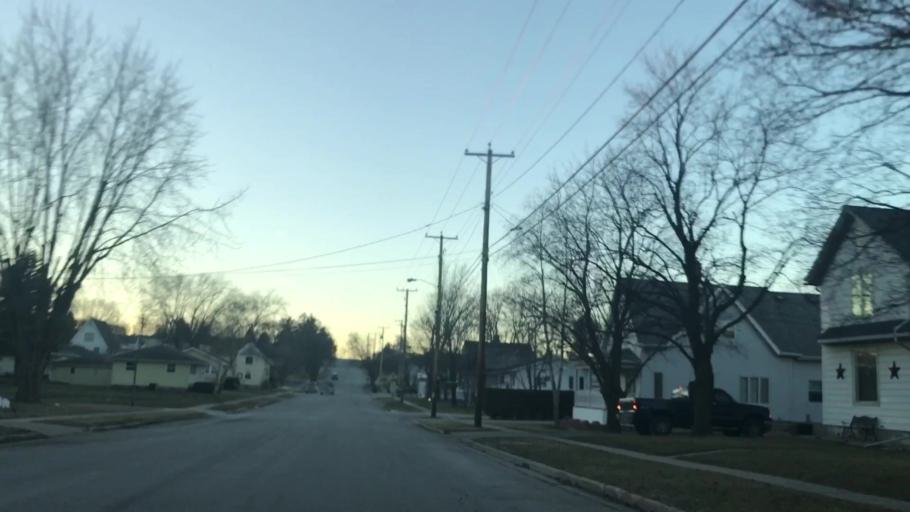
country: US
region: Wisconsin
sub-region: Dodge County
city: Mayville
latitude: 43.5012
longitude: -88.5495
